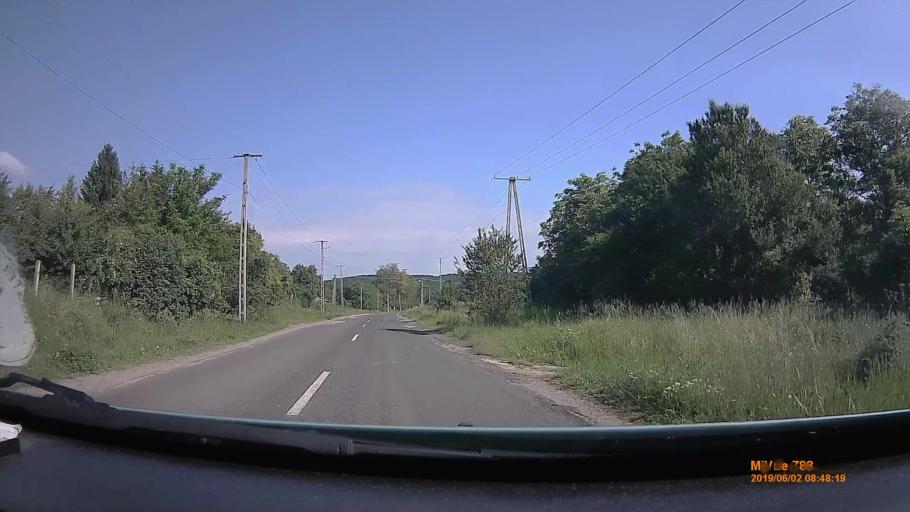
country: HU
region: Borsod-Abauj-Zemplen
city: Sajobabony
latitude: 48.1349
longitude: 20.7053
